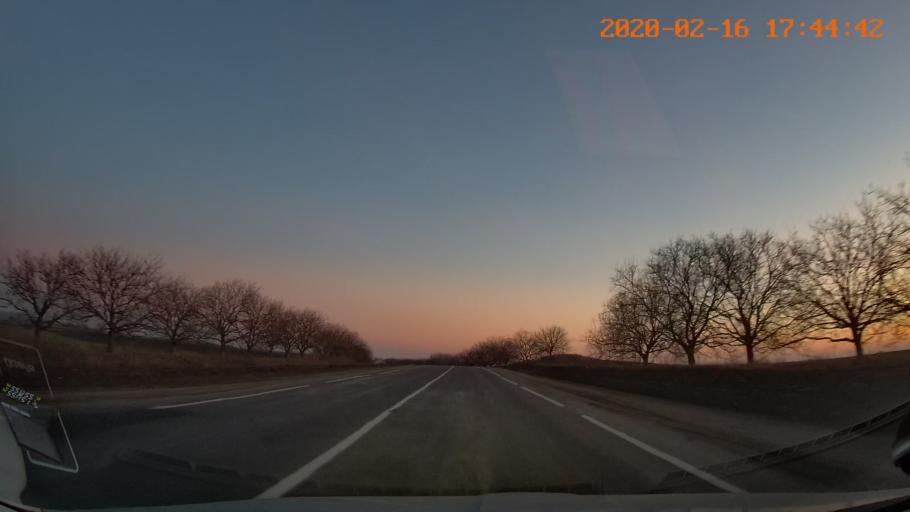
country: MD
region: Riscani
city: Riscani
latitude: 47.9934
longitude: 27.5730
